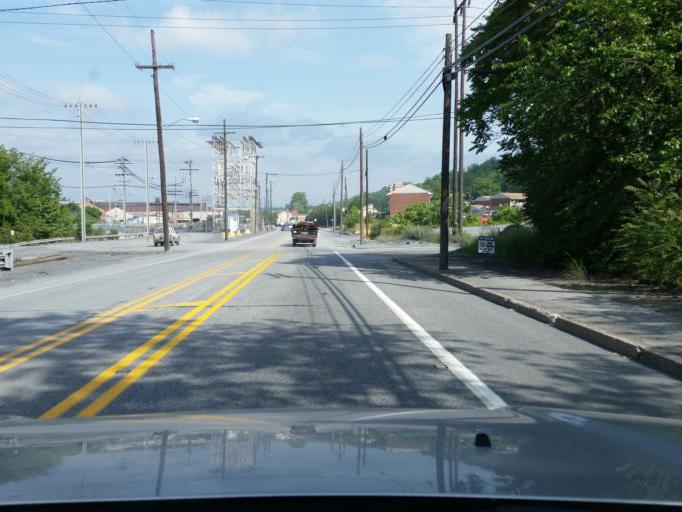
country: US
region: Pennsylvania
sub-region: Dauphin County
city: Bressler
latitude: 40.2219
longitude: -76.8240
